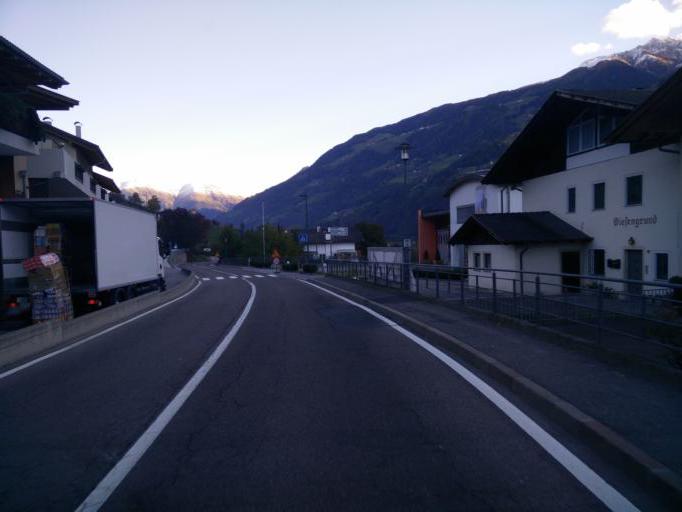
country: IT
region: Trentino-Alto Adige
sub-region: Bolzano
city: Rifiano
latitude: 46.7050
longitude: 11.1842
